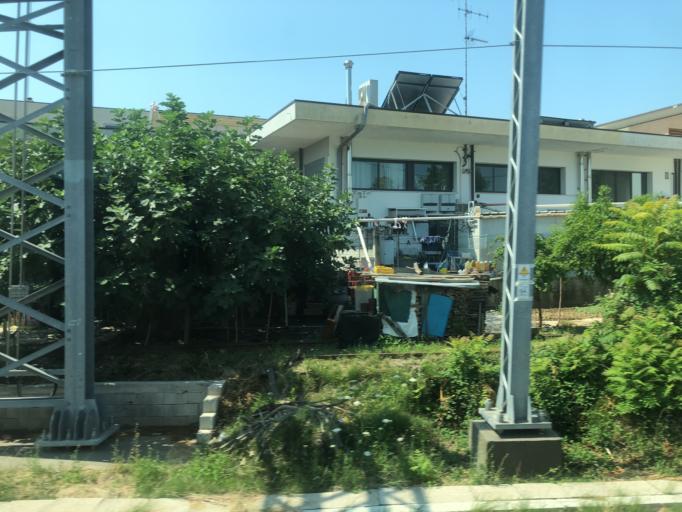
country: IT
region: Emilia-Romagna
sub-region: Forli-Cesena
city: Cesena
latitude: 44.1482
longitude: 12.2405
